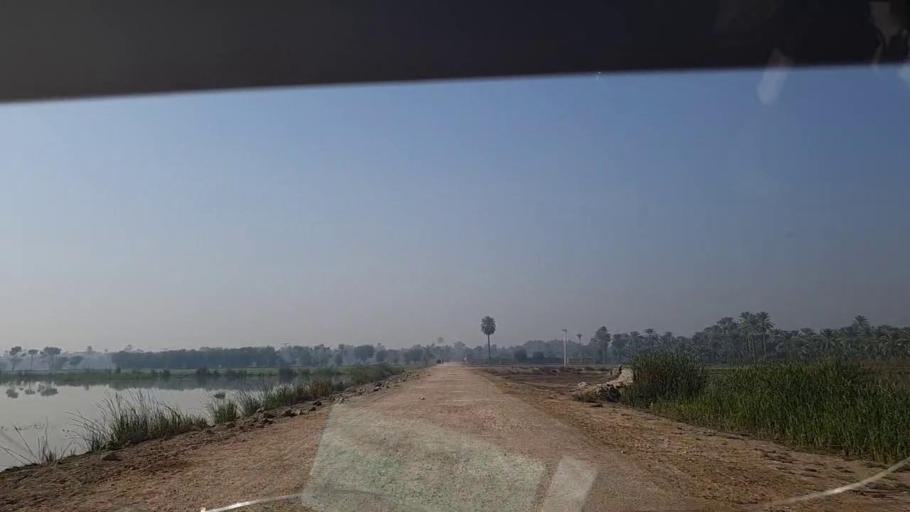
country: PK
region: Sindh
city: Khairpur
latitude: 27.4915
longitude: 68.7465
